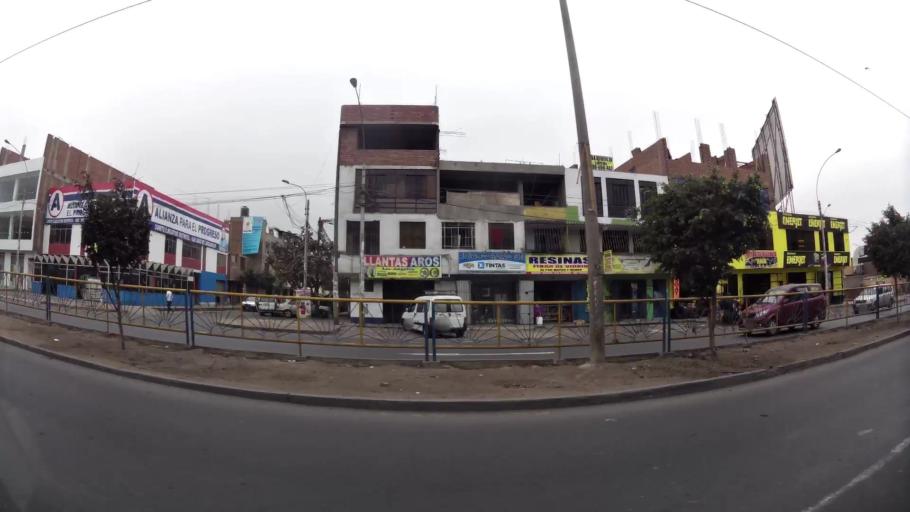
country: PE
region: Lima
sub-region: Lima
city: Independencia
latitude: -11.9881
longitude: -77.0092
